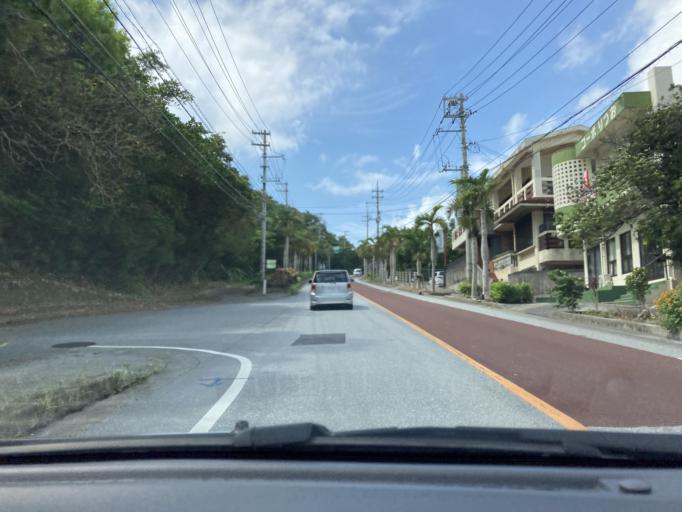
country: JP
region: Okinawa
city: Okinawa
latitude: 26.3016
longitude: 127.8037
